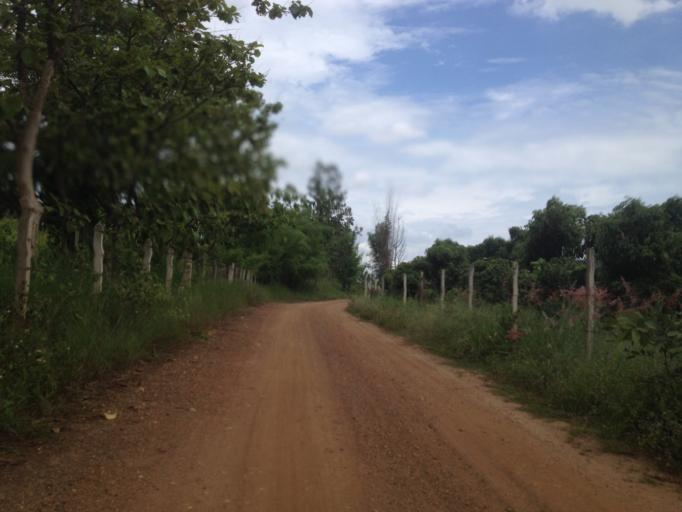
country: TH
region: Chiang Mai
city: Hang Dong
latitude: 18.7117
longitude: 98.8788
